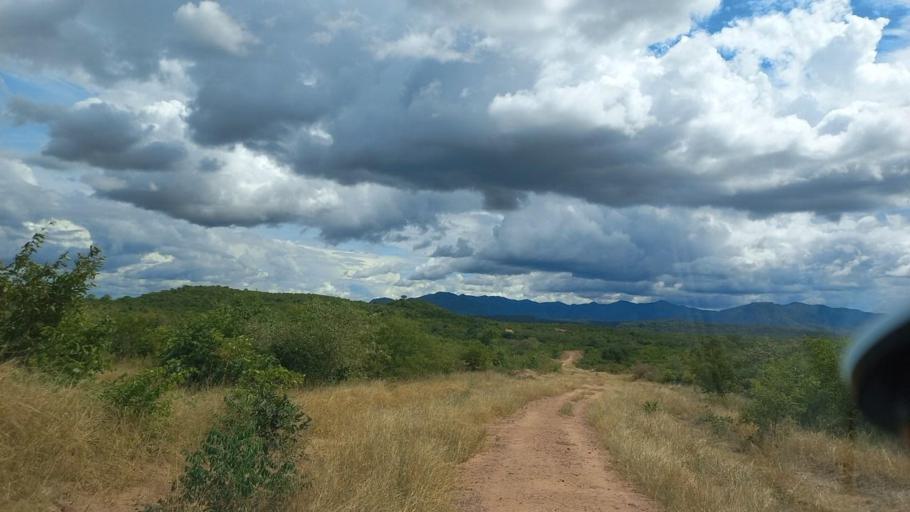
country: ZM
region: Lusaka
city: Luangwa
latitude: -15.6261
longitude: 30.3928
